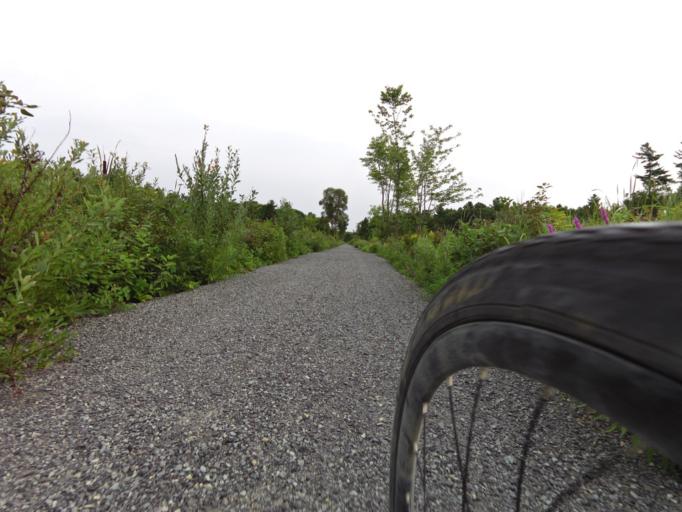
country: CA
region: Ontario
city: Gananoque
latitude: 44.5953
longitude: -76.3010
